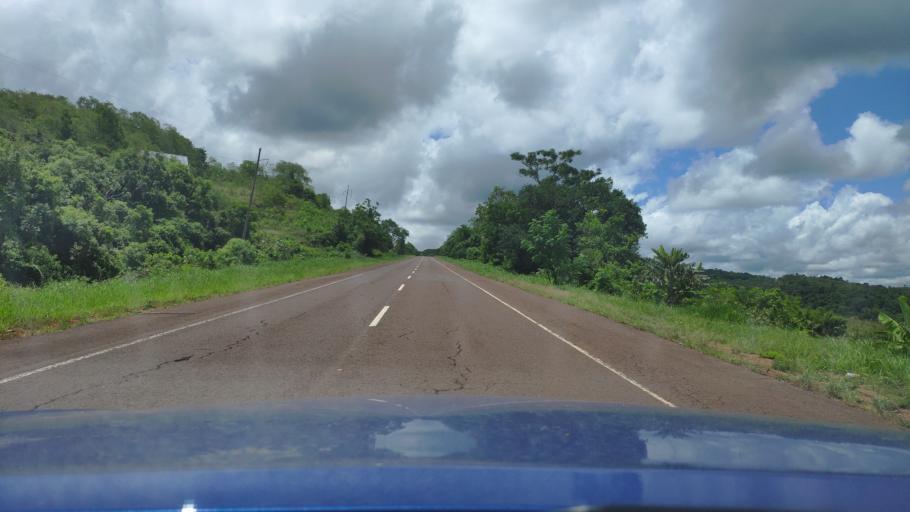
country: AR
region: Misiones
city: Dos Arroyos
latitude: -27.7596
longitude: -55.2485
